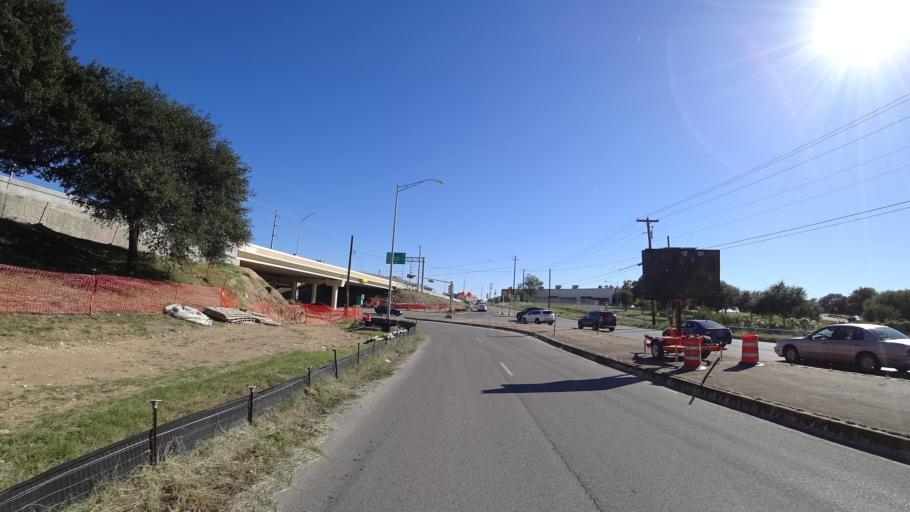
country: US
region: Texas
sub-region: Travis County
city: West Lake Hills
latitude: 30.3219
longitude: -97.7565
